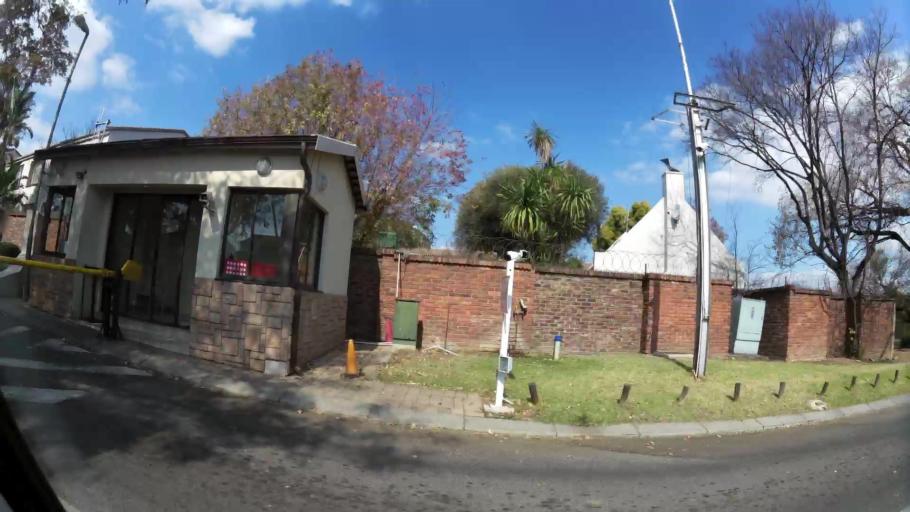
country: ZA
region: Gauteng
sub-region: City of Johannesburg Metropolitan Municipality
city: Midrand
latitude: -26.0306
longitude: 28.0782
